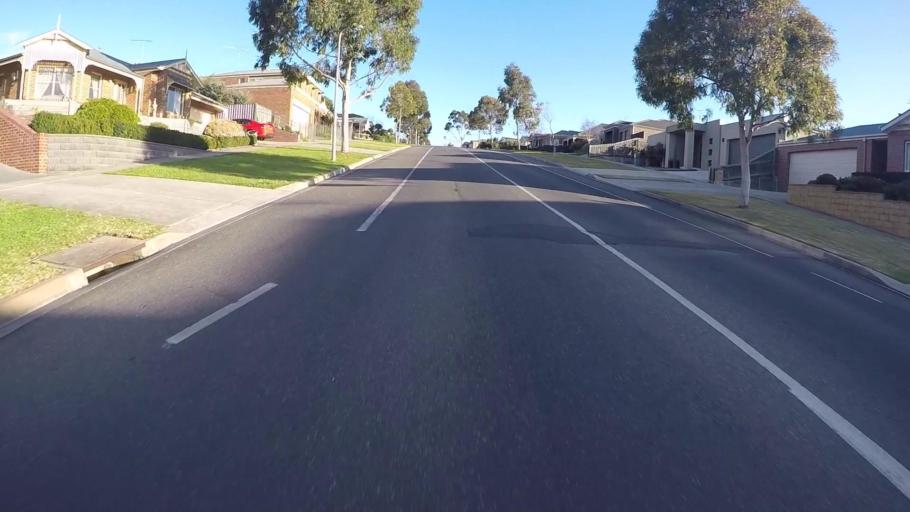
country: AU
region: Victoria
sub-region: Greater Geelong
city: Wandana Heights
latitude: -38.1635
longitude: 144.3017
